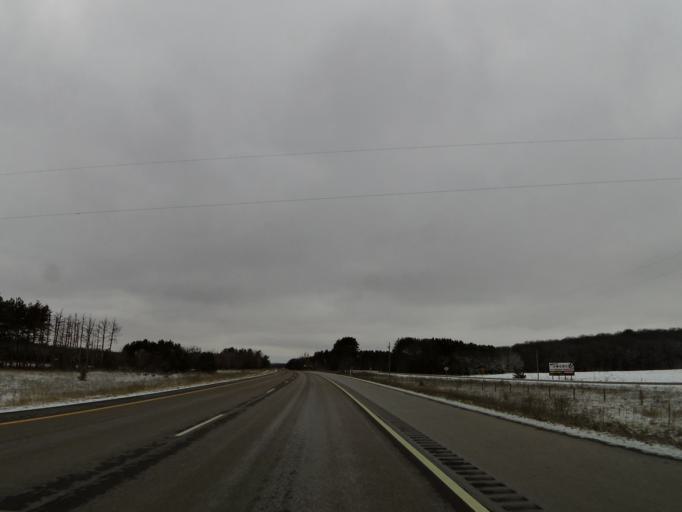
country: US
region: Wisconsin
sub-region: Trempealeau County
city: Osseo
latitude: 44.5479
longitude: -91.1629
